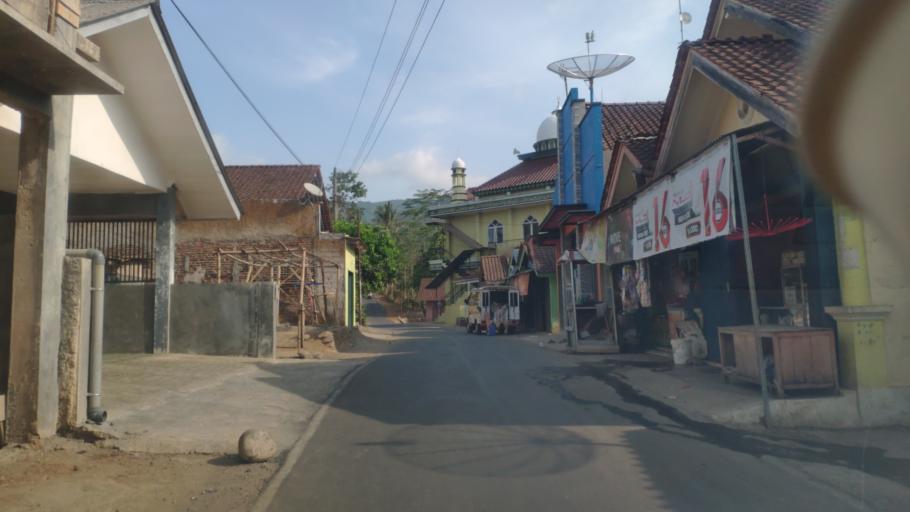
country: ID
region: Central Java
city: Wonosobo
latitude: -7.4019
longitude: 109.7294
